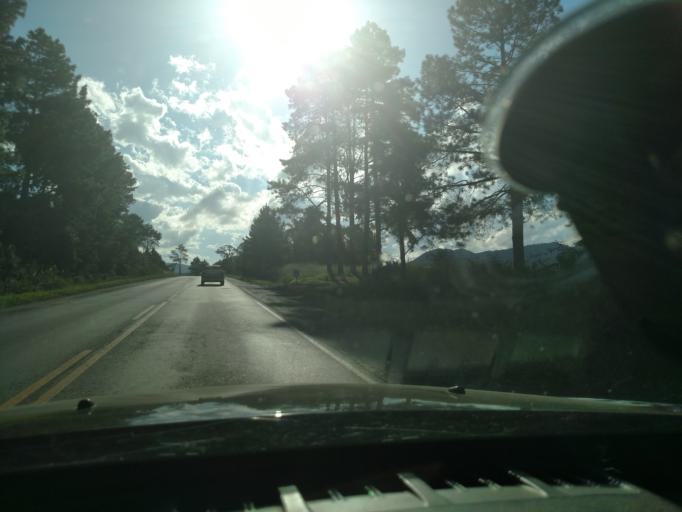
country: BR
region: Santa Catarina
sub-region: Otacilio Costa
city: Otacilio Costa
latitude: -27.3060
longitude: -50.1074
